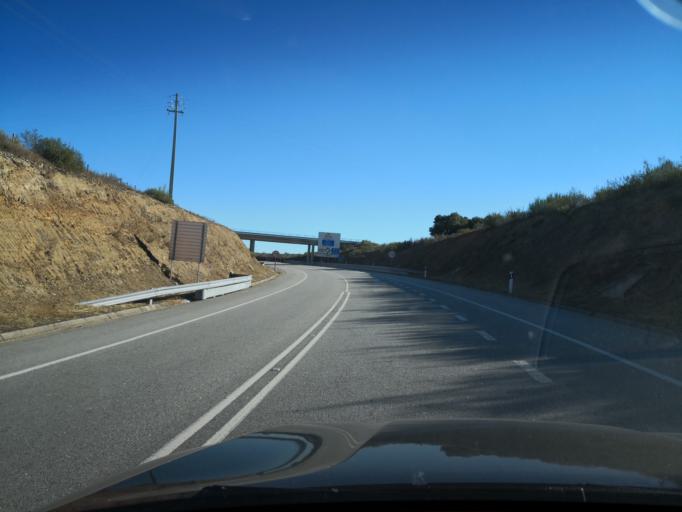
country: PT
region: Braganca
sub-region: Mirandela
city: Mirandela
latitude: 41.4811
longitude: -7.2246
